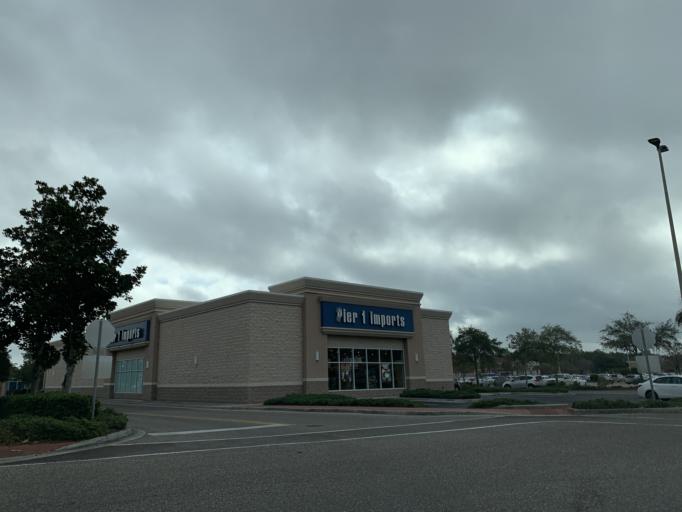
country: US
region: Florida
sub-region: Pinellas County
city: South Highpoint
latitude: 27.9599
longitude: -82.7259
